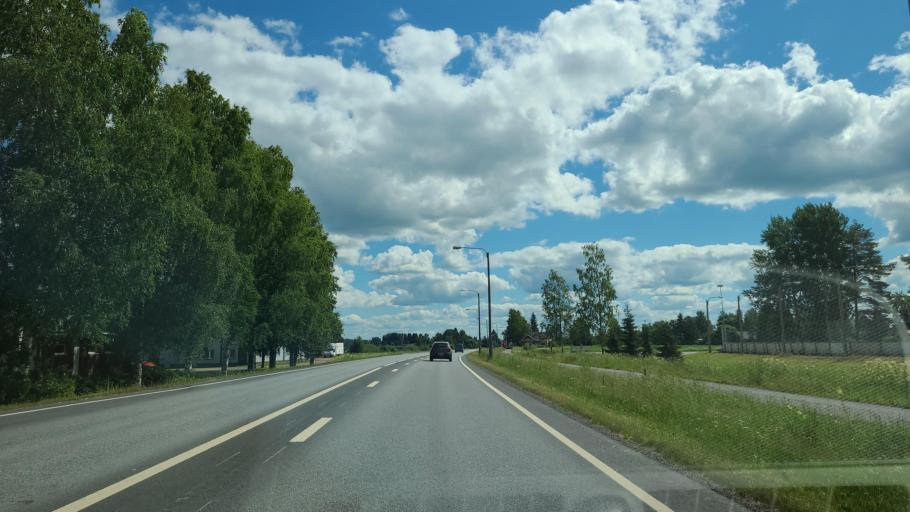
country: FI
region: Ostrobothnia
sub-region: Kyroenmaa
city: Isokyroe
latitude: 62.9733
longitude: 22.3820
